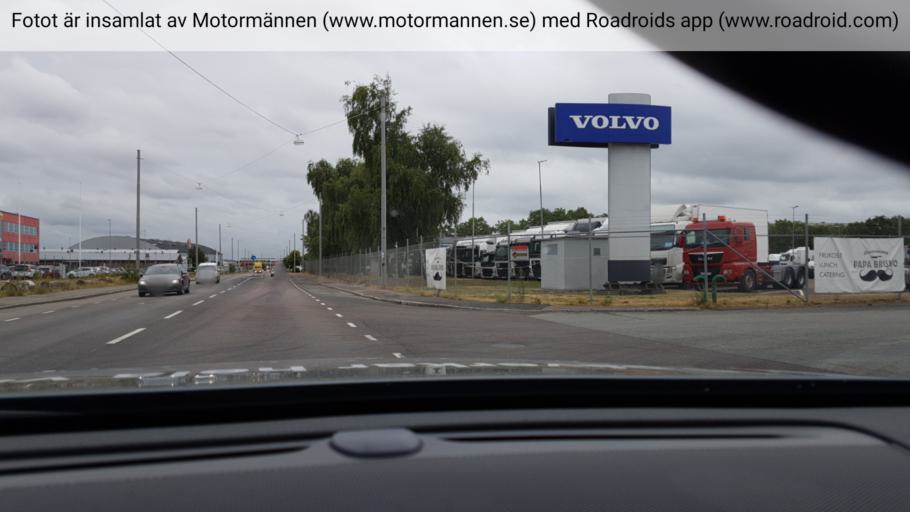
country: SE
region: Vaestra Goetaland
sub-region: Goteborg
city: Hammarkullen
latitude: 57.7534
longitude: 11.9958
